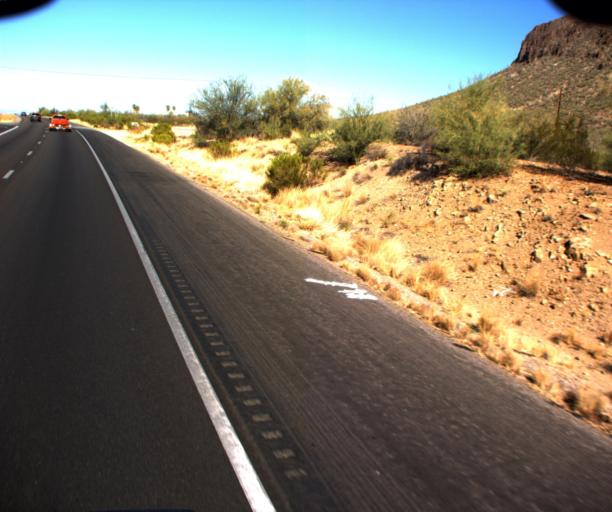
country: US
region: Arizona
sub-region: Pima County
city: Drexel Heights
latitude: 32.1775
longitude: -111.0490
